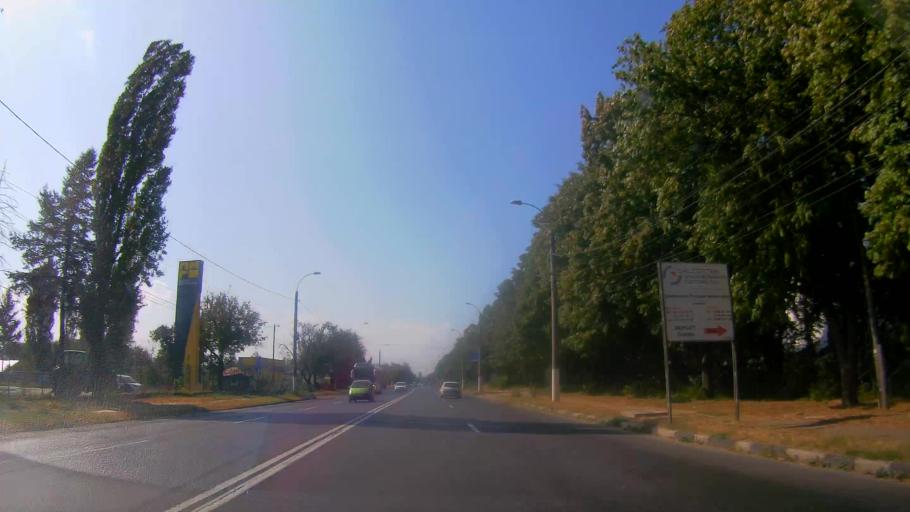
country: RO
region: Giurgiu
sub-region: Comuna Fratesti
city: Remus
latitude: 43.9230
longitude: 25.9739
